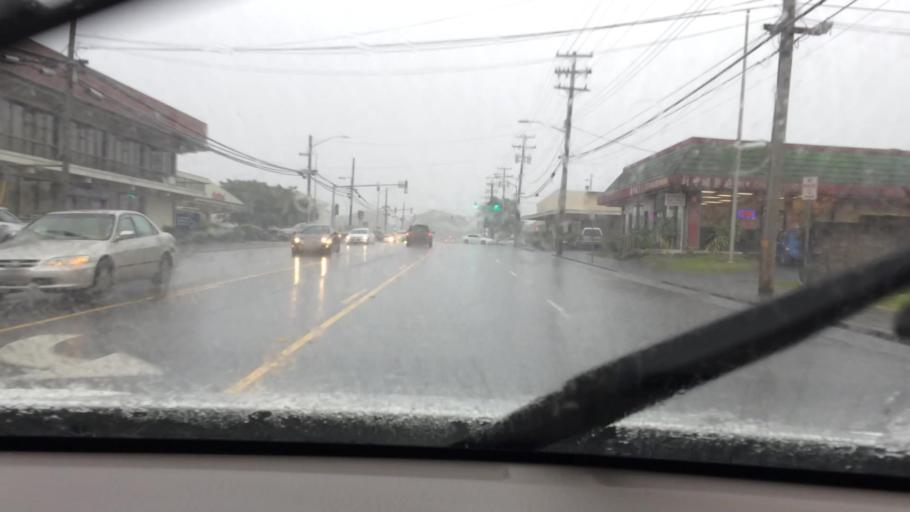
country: US
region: Hawaii
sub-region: Hawaii County
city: Hilo
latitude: 19.7193
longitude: -155.0820
